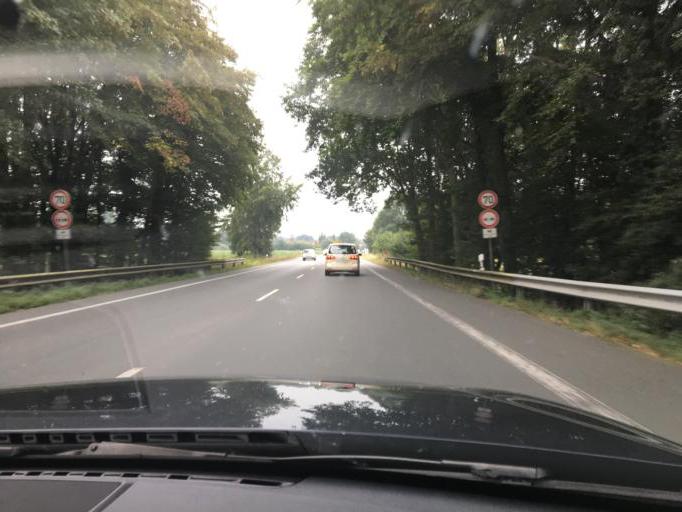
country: DE
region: North Rhine-Westphalia
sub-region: Regierungsbezirk Munster
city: Muenster
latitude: 52.0165
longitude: 7.6801
